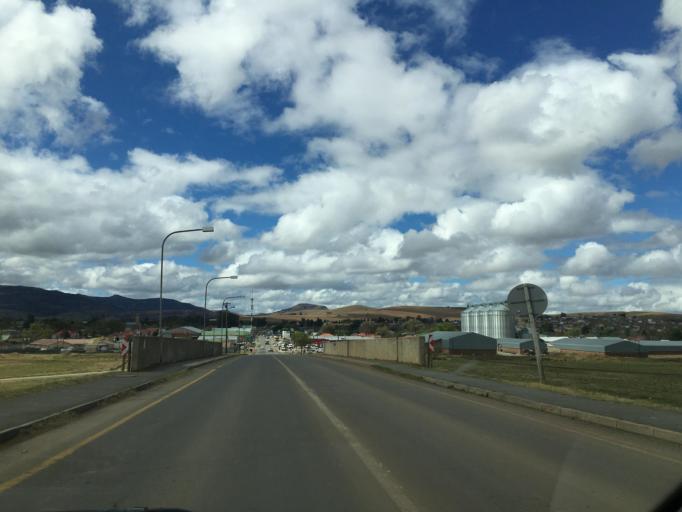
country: ZA
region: Eastern Cape
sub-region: Chris Hani District Municipality
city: Elliot
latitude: -31.3360
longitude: 27.8431
